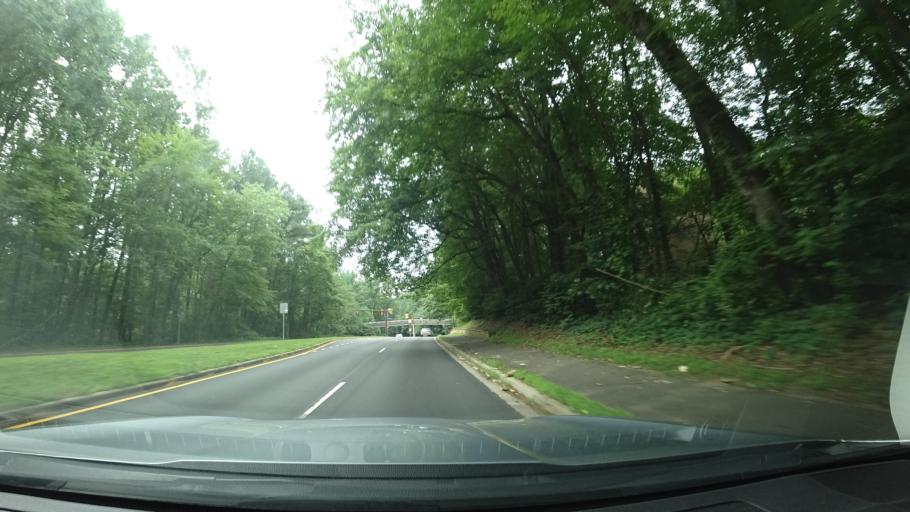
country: US
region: Virginia
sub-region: Fairfax County
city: Reston
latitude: 38.9708
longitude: -77.3334
